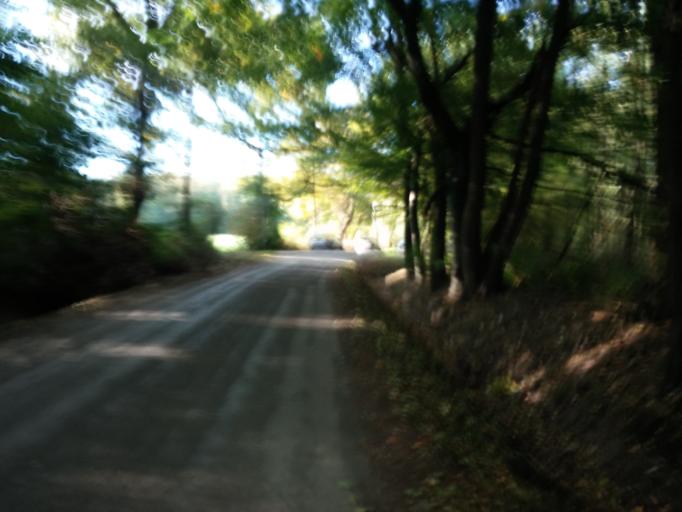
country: DE
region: North Rhine-Westphalia
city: Dorsten
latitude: 51.6229
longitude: 6.9916
